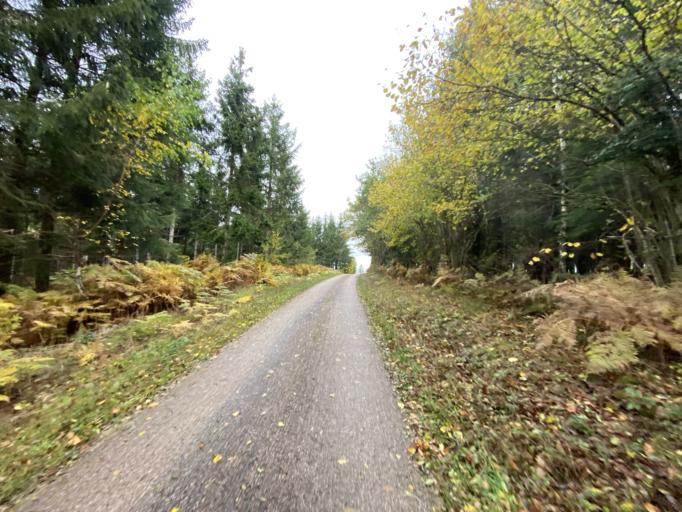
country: FR
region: Bourgogne
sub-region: Departement de la Cote-d'Or
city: Saulieu
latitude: 47.2658
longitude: 4.1662
